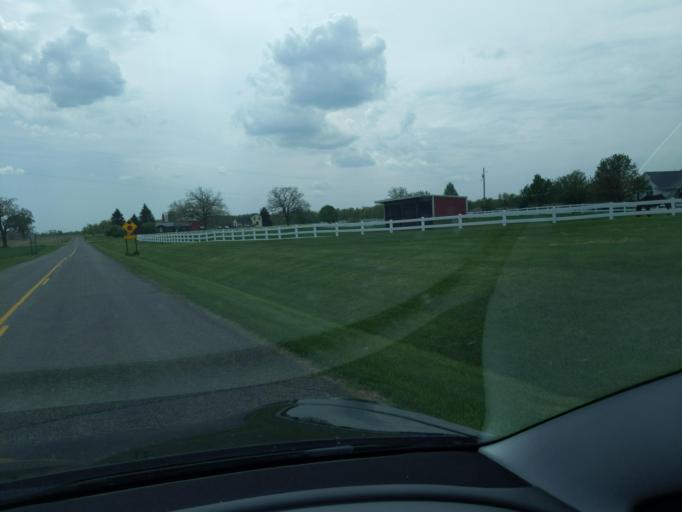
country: US
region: Michigan
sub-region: Ingham County
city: Leslie
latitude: 42.4917
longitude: -84.3317
